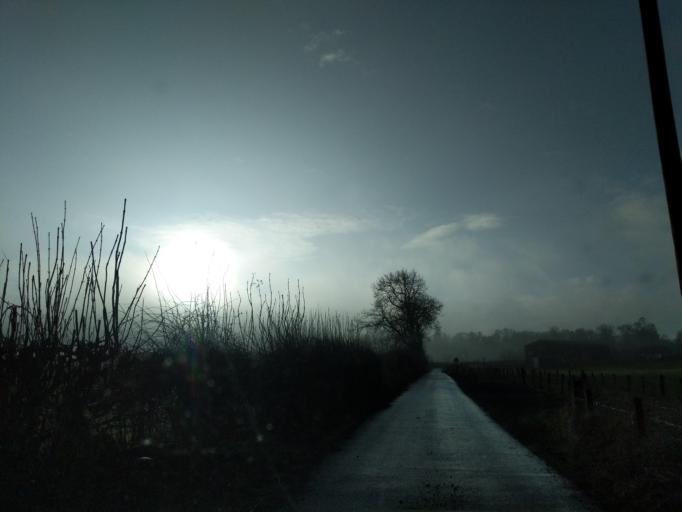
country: GB
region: Scotland
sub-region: Perth and Kinross
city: Auchterarder
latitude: 56.2910
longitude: -3.6928
